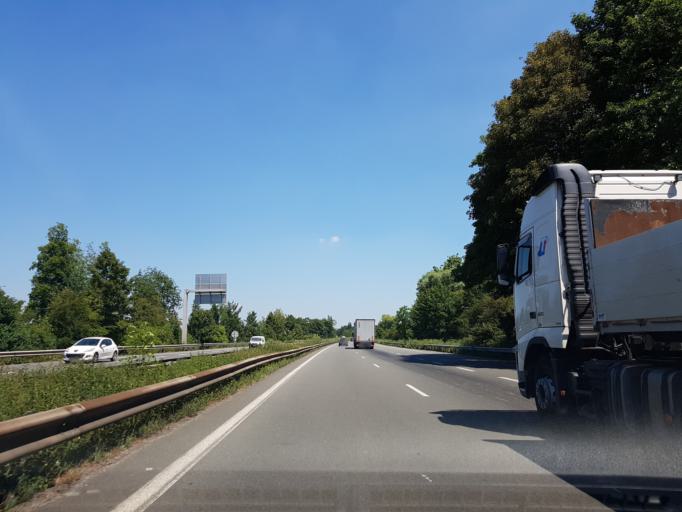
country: FR
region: Nord-Pas-de-Calais
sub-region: Departement du Nord
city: Lieu-Saint-Amand
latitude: 50.2705
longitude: 3.3344
